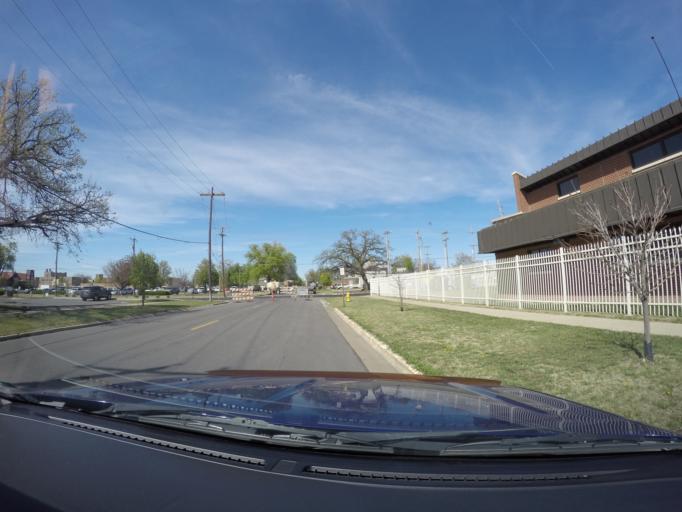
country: US
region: Kansas
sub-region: Saline County
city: Salina
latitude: 38.8340
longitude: -97.6079
